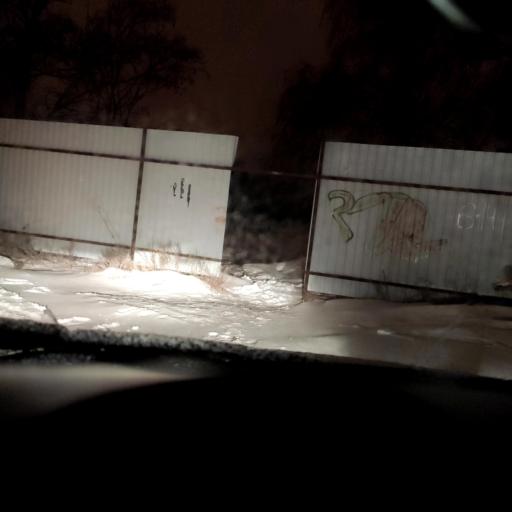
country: RU
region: Voronezj
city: Podgornoye
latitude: 51.7287
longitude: 39.1632
